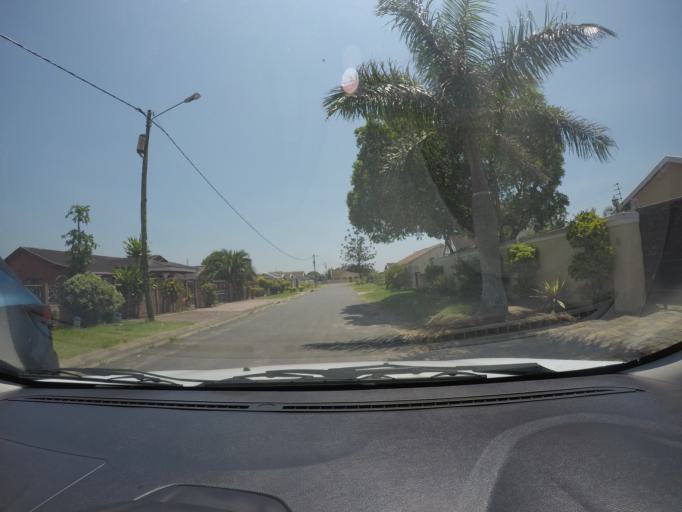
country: ZA
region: KwaZulu-Natal
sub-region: uThungulu District Municipality
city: eSikhawini
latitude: -28.8711
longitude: 31.9130
